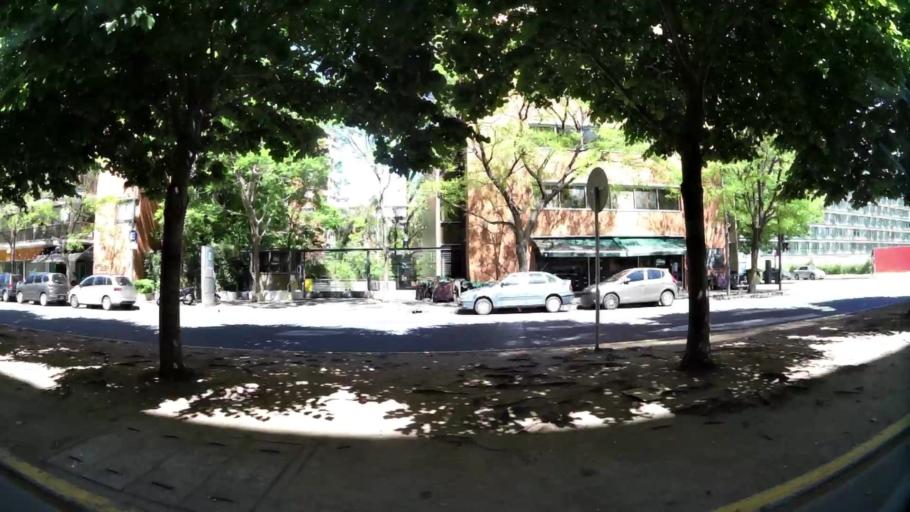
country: AR
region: Buenos Aires F.D.
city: Buenos Aires
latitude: -34.6164
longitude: -58.3620
